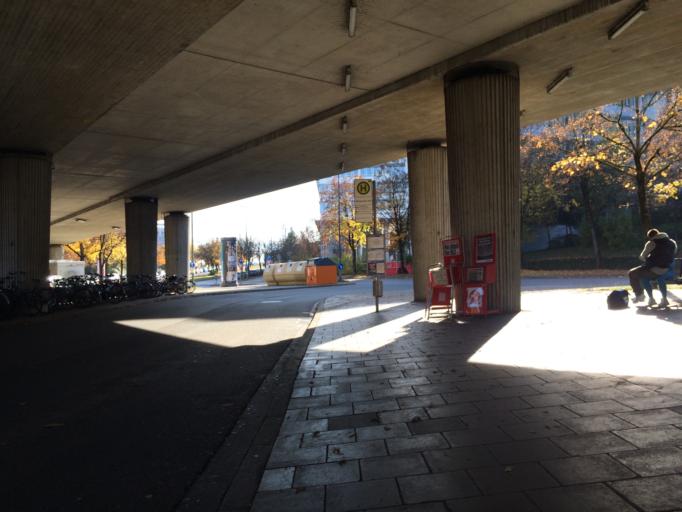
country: DE
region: Bavaria
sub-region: Upper Bavaria
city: Neubiberg
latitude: 48.0891
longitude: 11.6449
